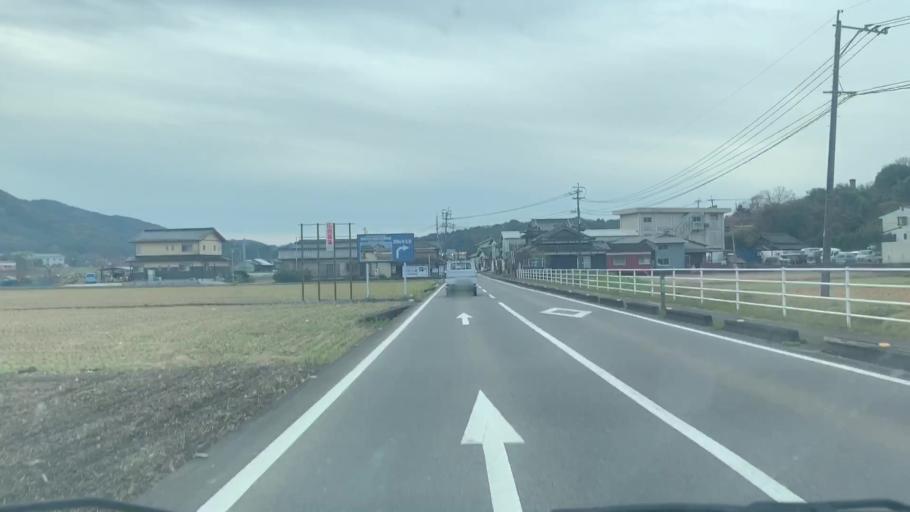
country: JP
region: Saga Prefecture
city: Takeocho-takeo
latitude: 33.1587
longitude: 130.0626
